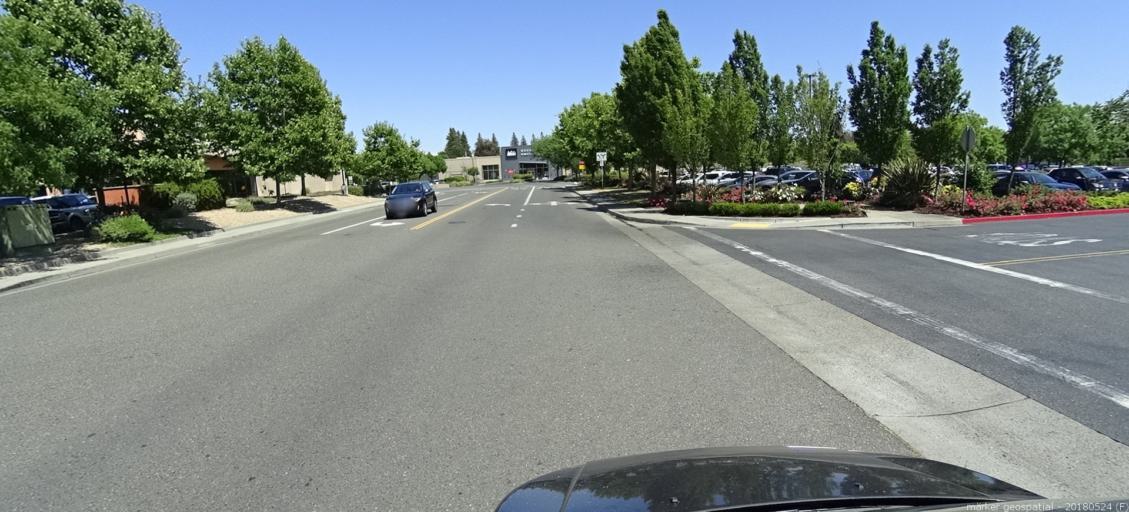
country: US
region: California
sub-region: Sacramento County
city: Sacramento
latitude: 38.5978
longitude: -121.4517
